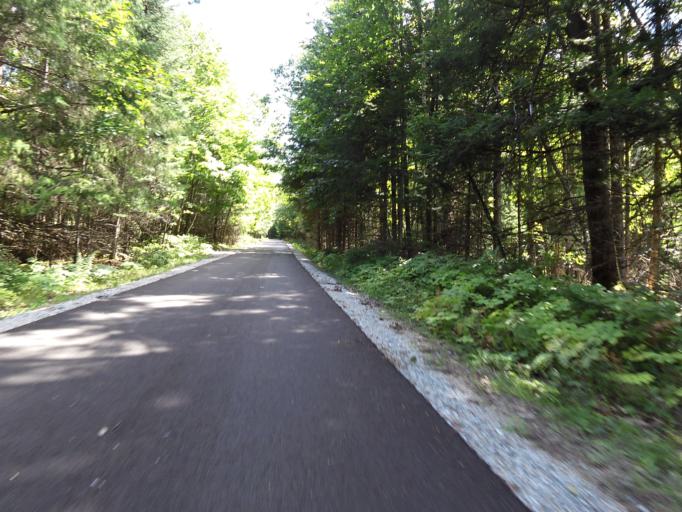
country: CA
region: Quebec
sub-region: Outaouais
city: Maniwaki
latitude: 46.1433
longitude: -76.0401
